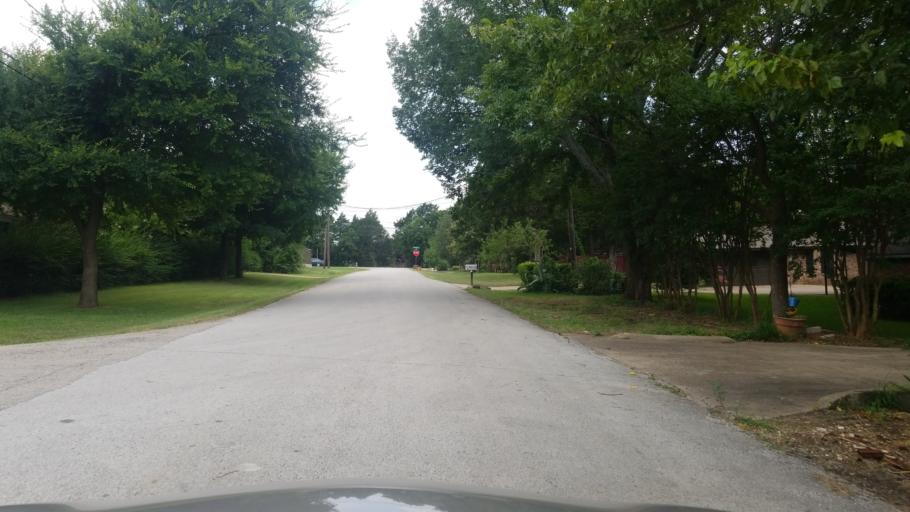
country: US
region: Texas
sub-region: Dallas County
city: Duncanville
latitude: 32.6846
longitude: -96.9327
